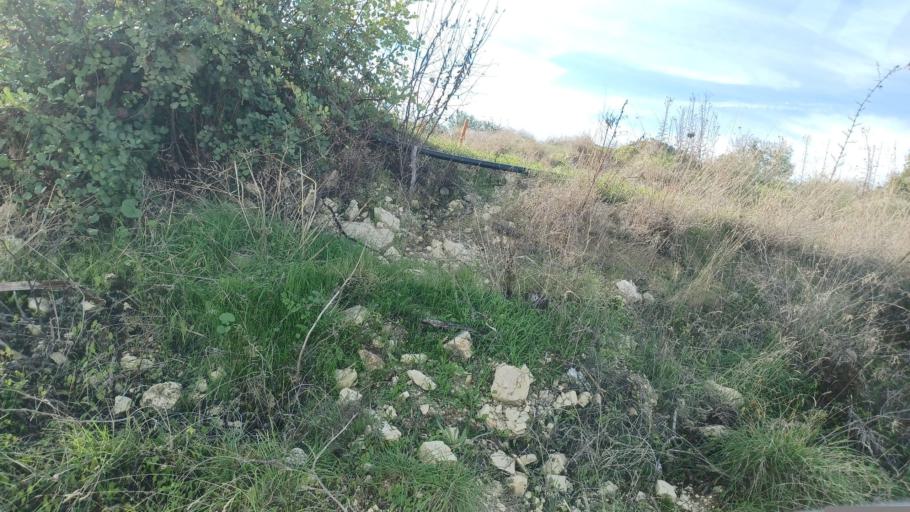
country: CY
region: Pafos
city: Mesogi
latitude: 34.8612
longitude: 32.5202
